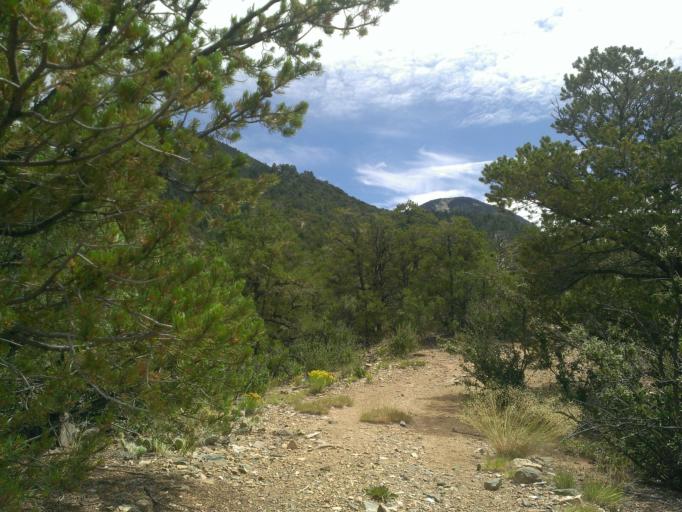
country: US
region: New Mexico
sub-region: Taos County
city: Arroyo Seco
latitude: 36.5357
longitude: -105.5595
